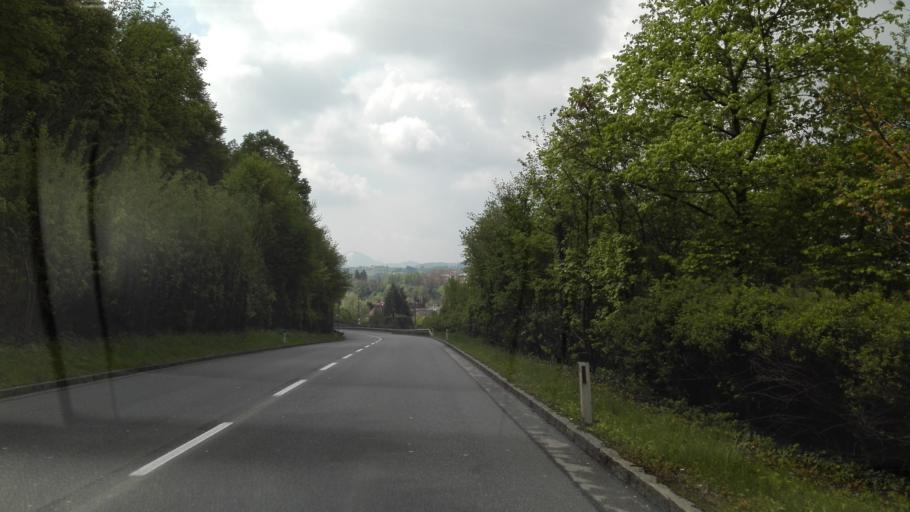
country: AT
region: Upper Austria
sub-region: Steyr Stadt
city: Steyr
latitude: 48.0358
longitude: 14.4211
